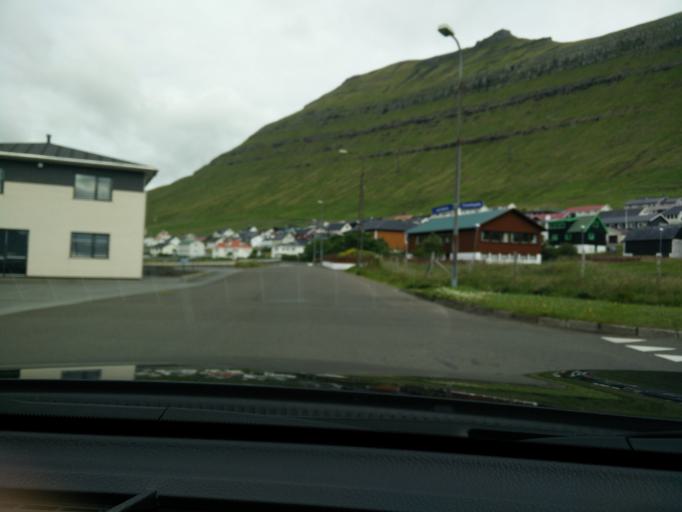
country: FO
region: Eysturoy
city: Eystur
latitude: 62.1990
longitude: -6.7432
